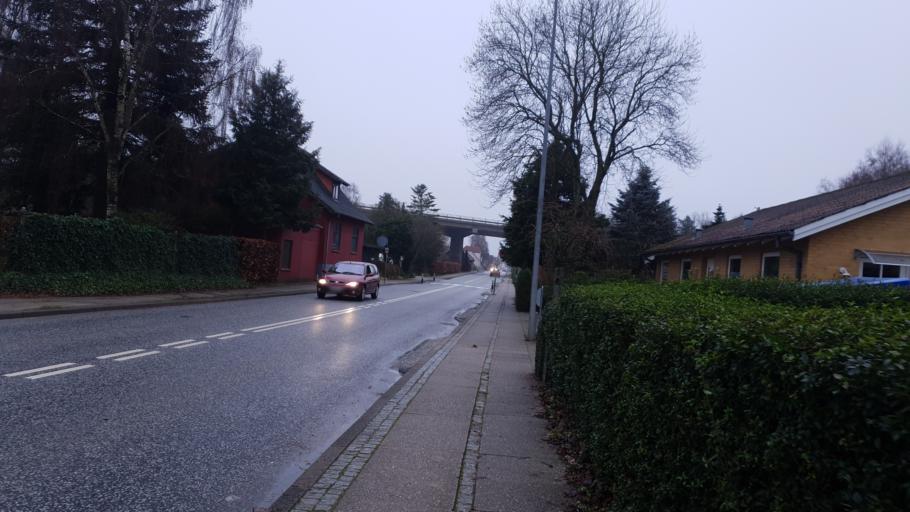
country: DK
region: Central Jutland
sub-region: Hedensted Kommune
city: Hedensted
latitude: 55.7745
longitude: 9.6983
